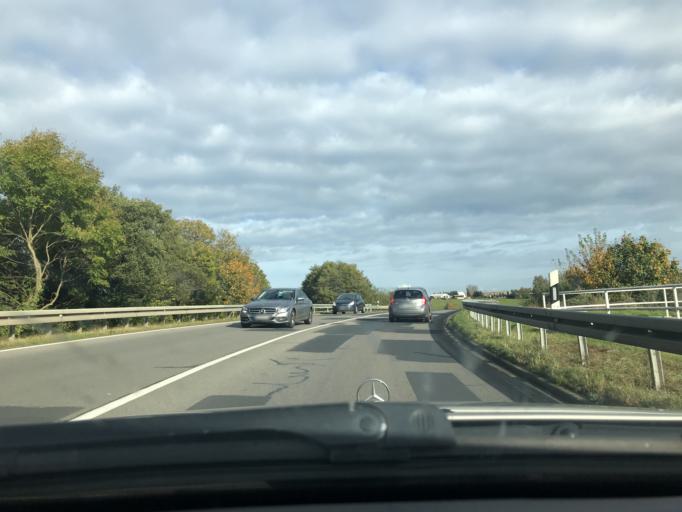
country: DE
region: Mecklenburg-Vorpommern
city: Wolgast
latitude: 54.0568
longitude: 13.7912
